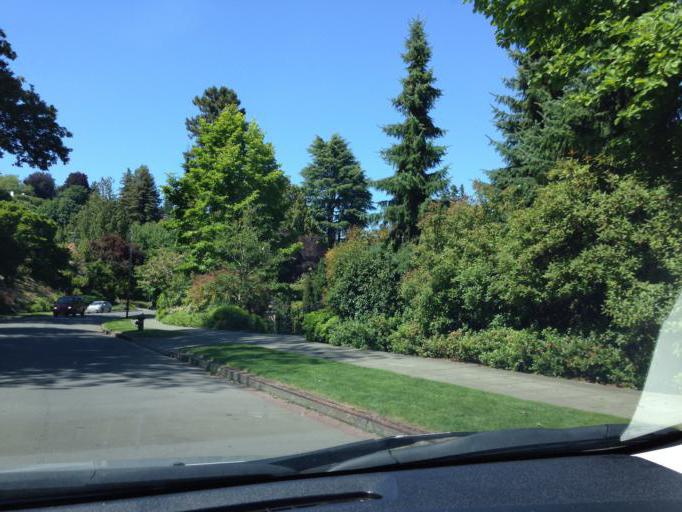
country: US
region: Washington
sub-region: King County
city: Seattle
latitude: 47.6228
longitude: -122.2840
